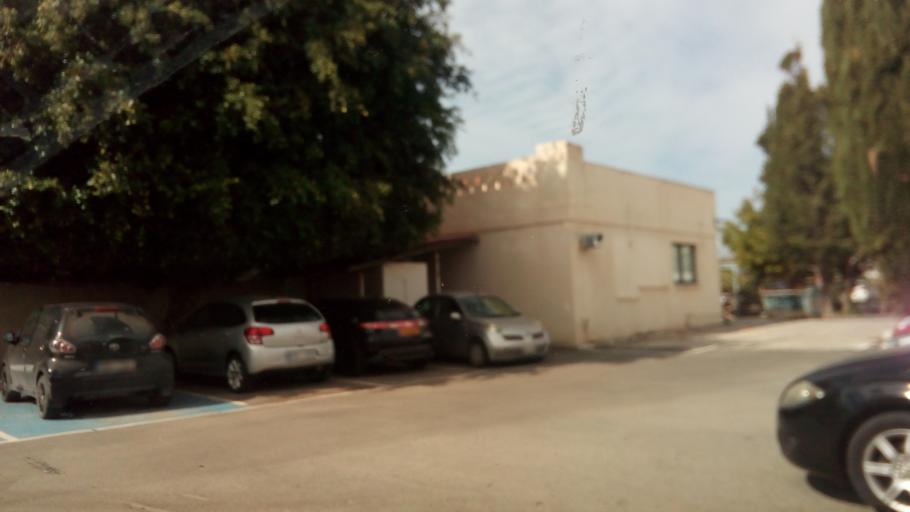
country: CY
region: Pafos
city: Paphos
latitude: 34.7497
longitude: 32.4271
